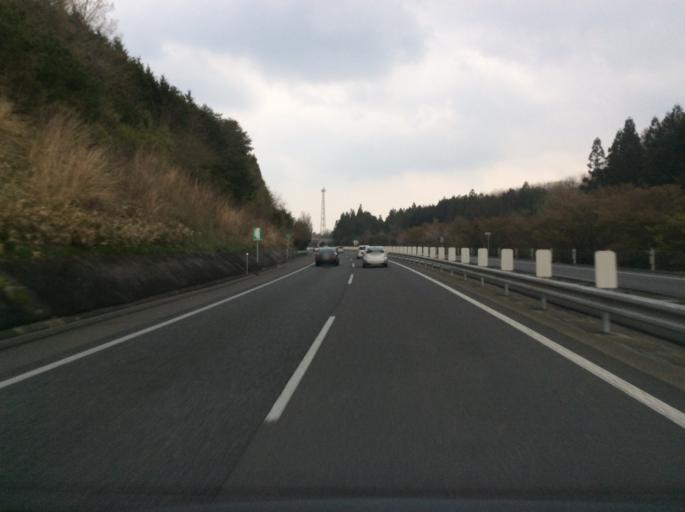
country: JP
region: Fukushima
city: Ishikawa
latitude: 37.2249
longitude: 140.6851
